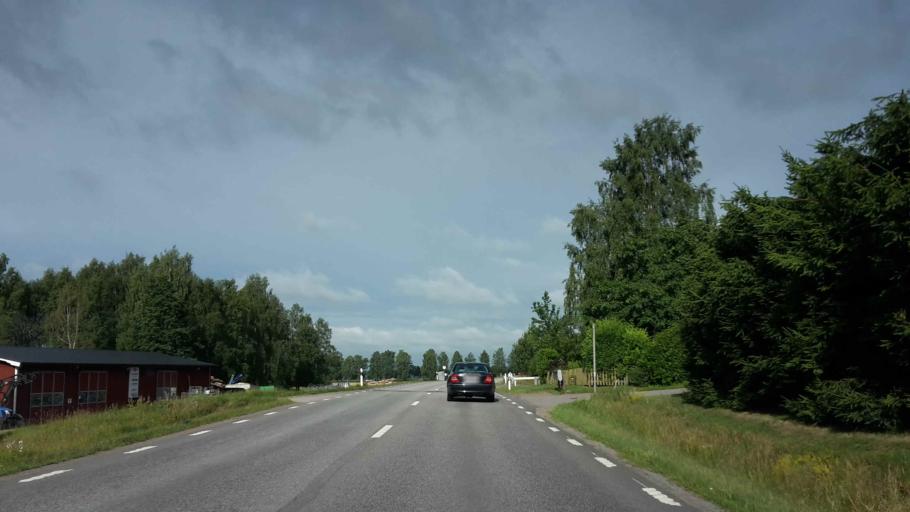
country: SE
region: OEstergoetland
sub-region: Motala Kommun
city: Borensberg
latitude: 58.5719
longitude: 15.2290
